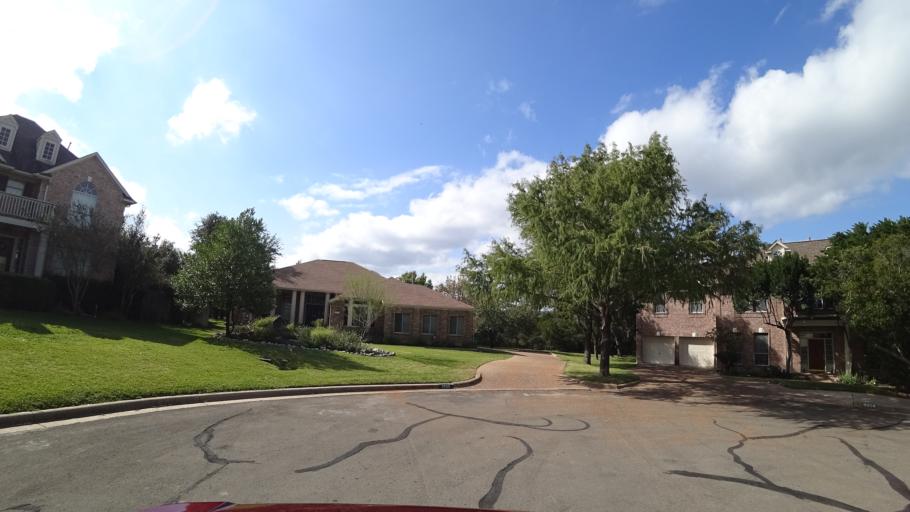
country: US
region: Texas
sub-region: Williamson County
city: Jollyville
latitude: 30.4181
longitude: -97.7923
